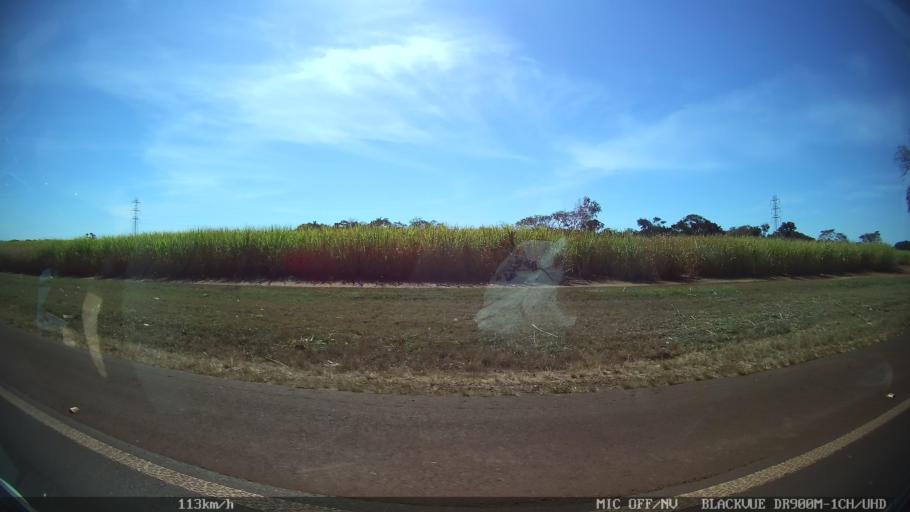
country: BR
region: Sao Paulo
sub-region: Guaira
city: Guaira
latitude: -20.4453
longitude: -48.2240
